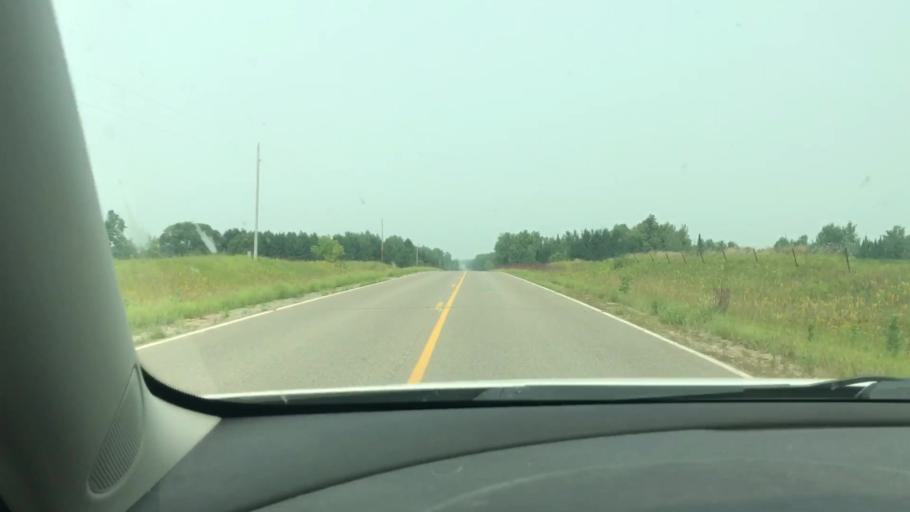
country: US
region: Minnesota
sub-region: Itasca County
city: Cohasset
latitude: 47.3768
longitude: -93.8803
